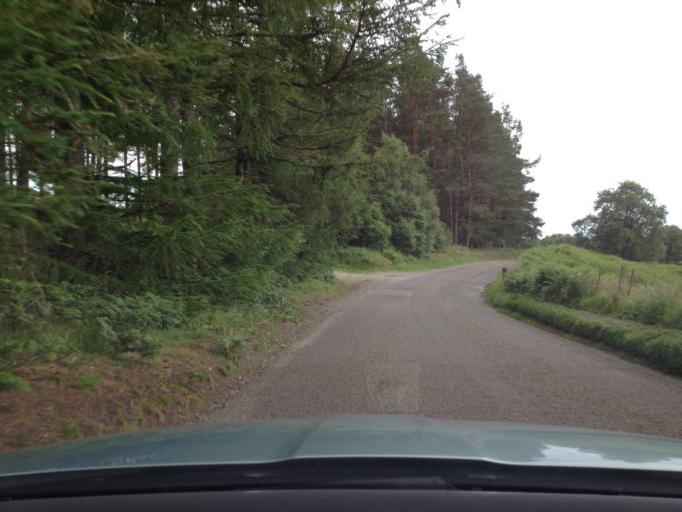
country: GB
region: Scotland
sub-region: Angus
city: Brechin
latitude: 56.8546
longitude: -2.6811
